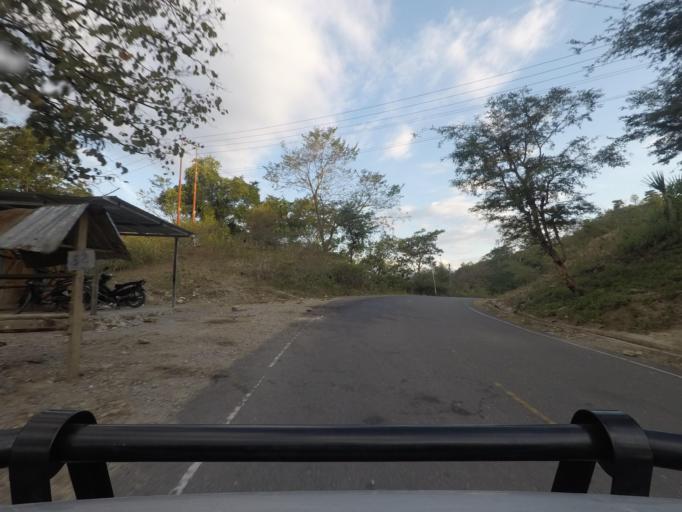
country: TL
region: Bobonaro
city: Maliana
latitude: -8.9550
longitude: 125.1095
